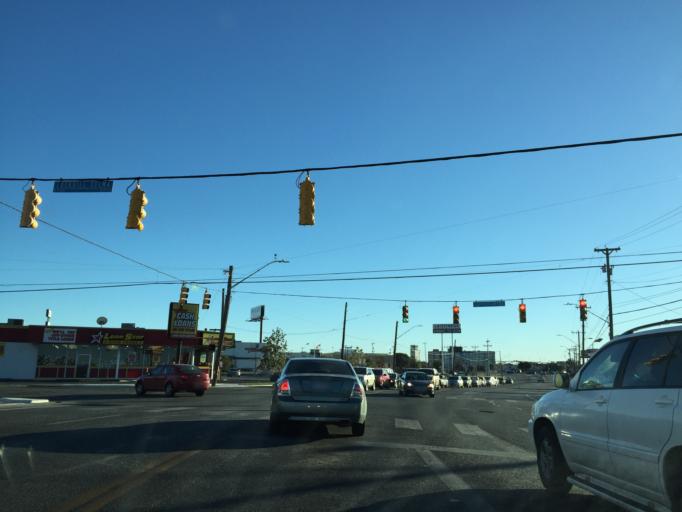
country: US
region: Texas
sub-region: Bexar County
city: Castle Hills
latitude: 29.5234
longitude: -98.5050
